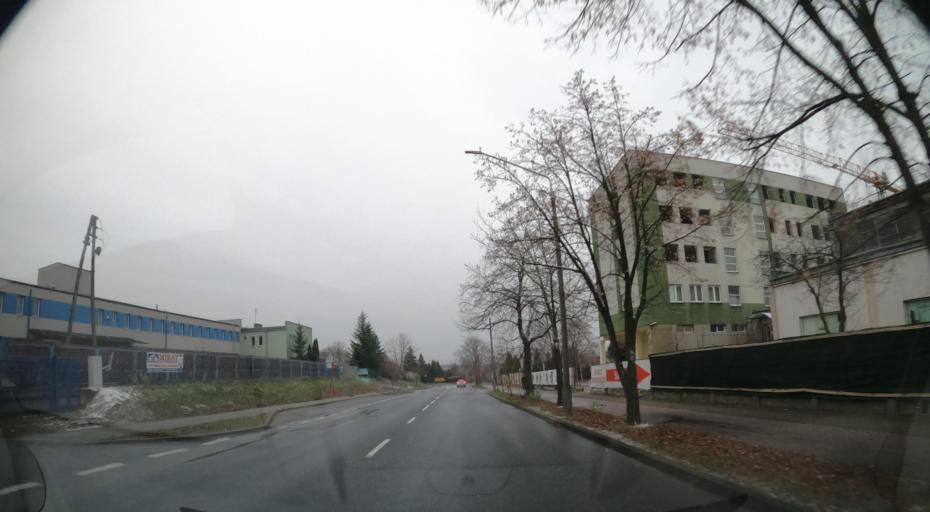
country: PL
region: Masovian Voivodeship
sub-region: Powiat radomski
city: Trablice
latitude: 51.3812
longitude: 21.1214
